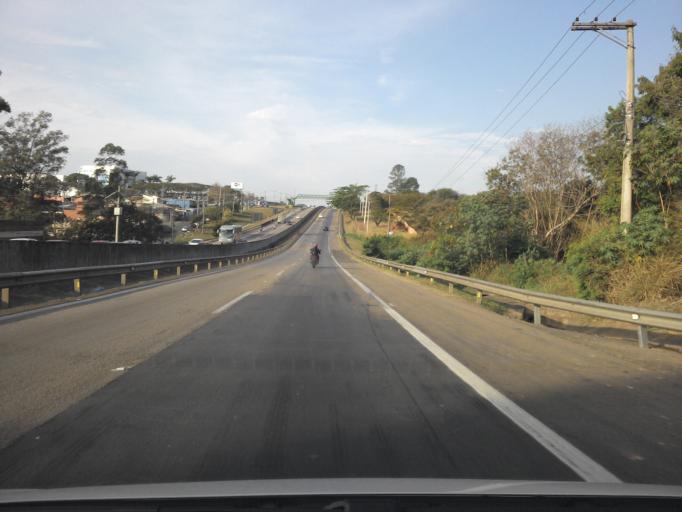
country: BR
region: Sao Paulo
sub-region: Hortolandia
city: Hortolandia
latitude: -22.8985
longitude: -47.1938
